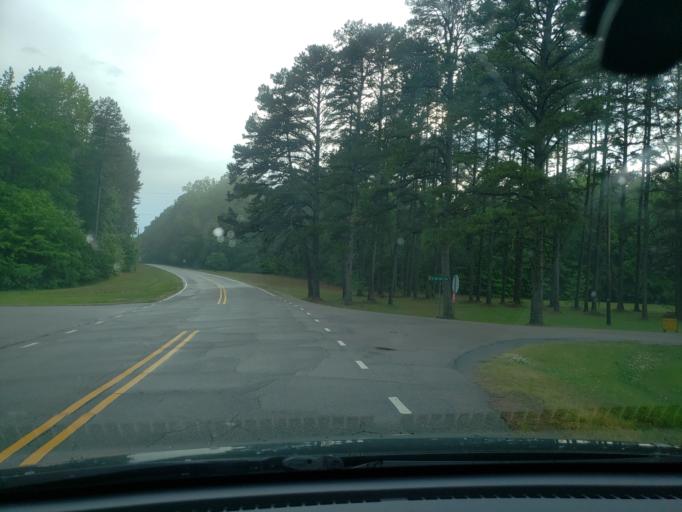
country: US
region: North Carolina
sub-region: Vance County
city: Henderson
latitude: 36.4100
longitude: -78.3989
